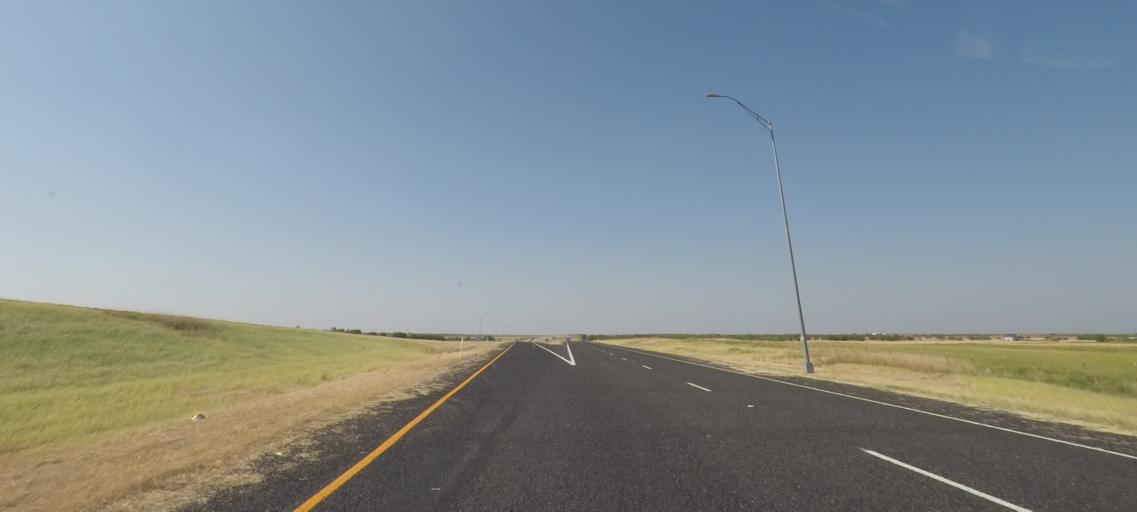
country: US
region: Texas
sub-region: Baylor County
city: Seymour
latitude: 33.5982
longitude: -99.2409
